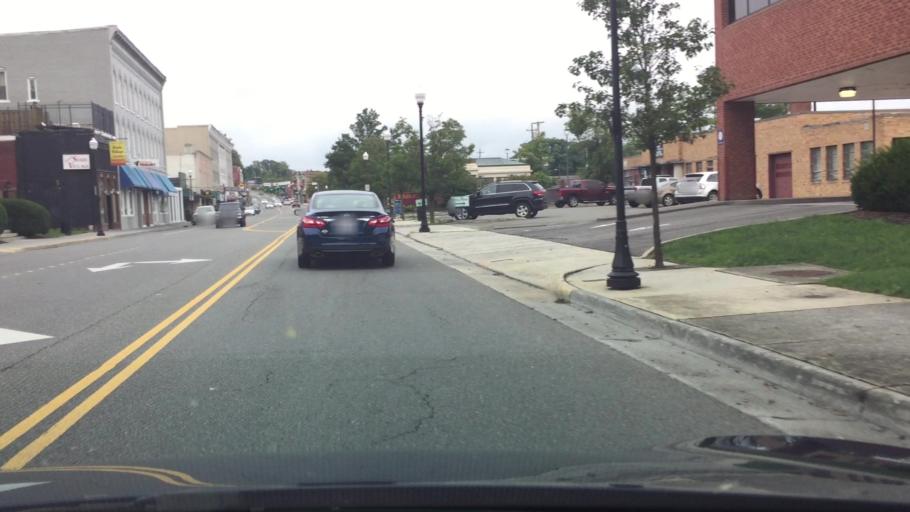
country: US
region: Virginia
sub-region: City of Radford
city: Radford
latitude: 37.1413
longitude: -80.5541
